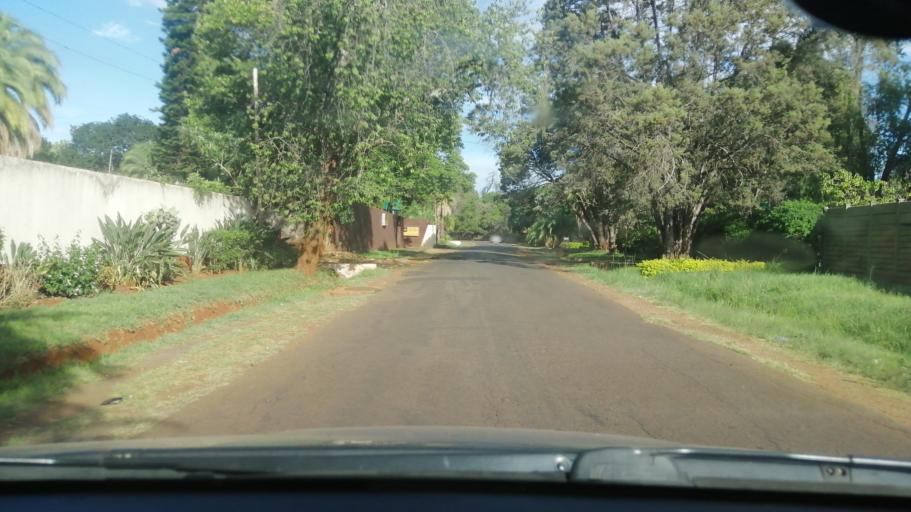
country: ZW
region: Harare
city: Harare
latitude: -17.7647
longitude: 31.0544
